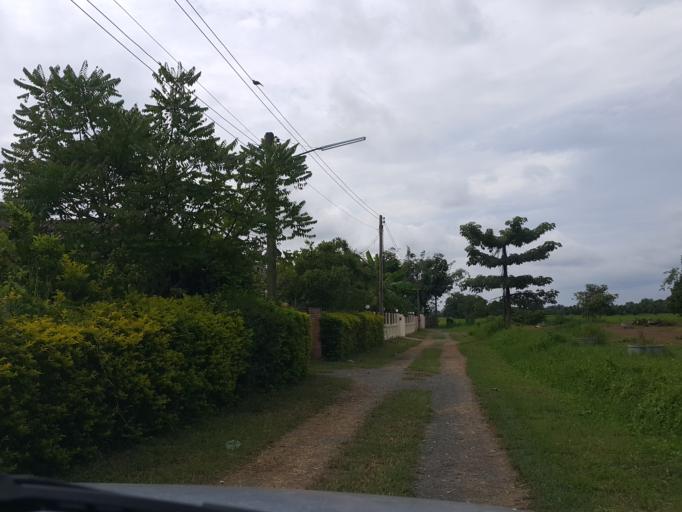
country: TH
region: Chiang Mai
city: San Sai
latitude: 18.8422
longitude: 99.1408
